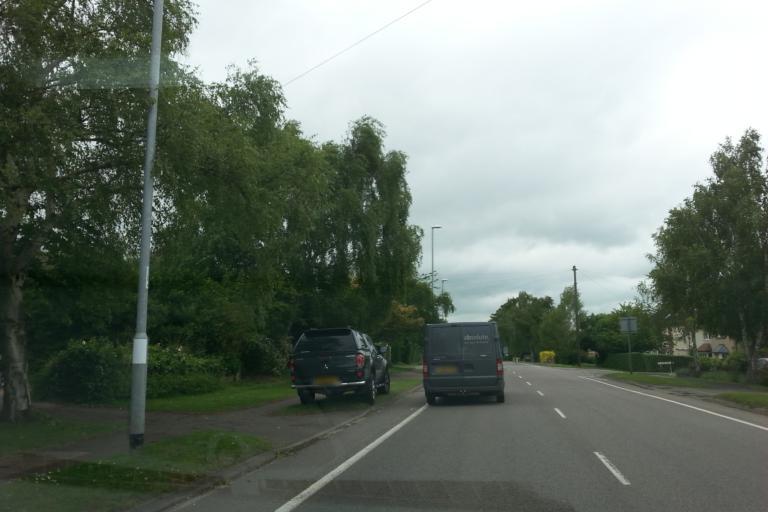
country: GB
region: England
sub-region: Cambridgeshire
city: Cambridge
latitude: 52.1560
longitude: 0.1293
